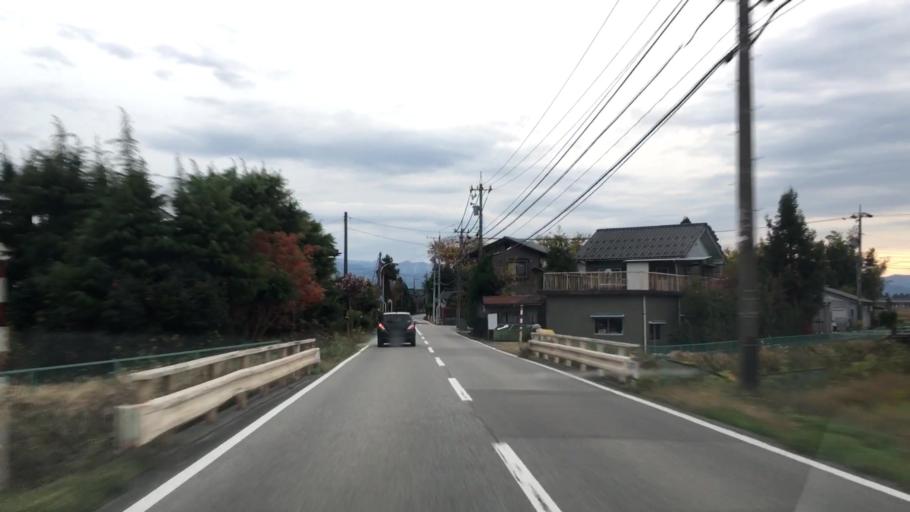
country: JP
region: Toyama
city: Kamiichi
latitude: 36.6948
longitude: 137.3151
